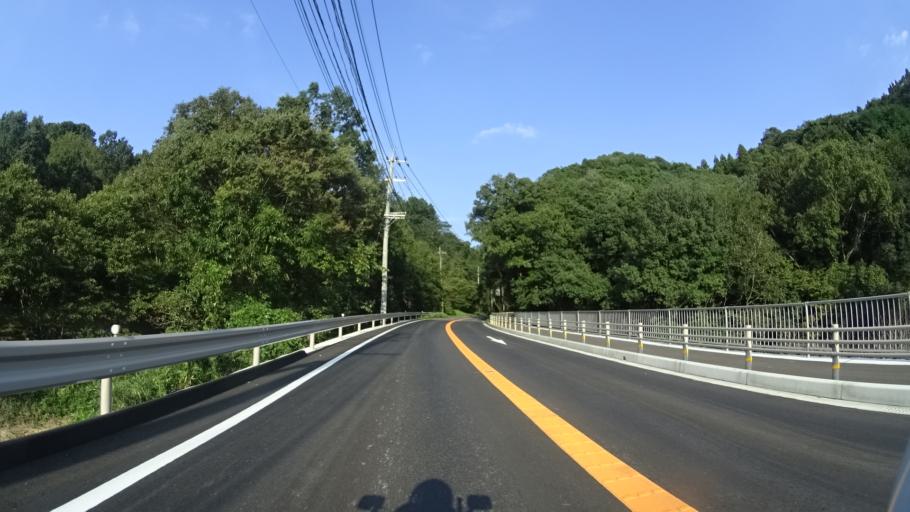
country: JP
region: Oita
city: Bungo-Takada-shi
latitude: 33.4458
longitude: 131.3349
